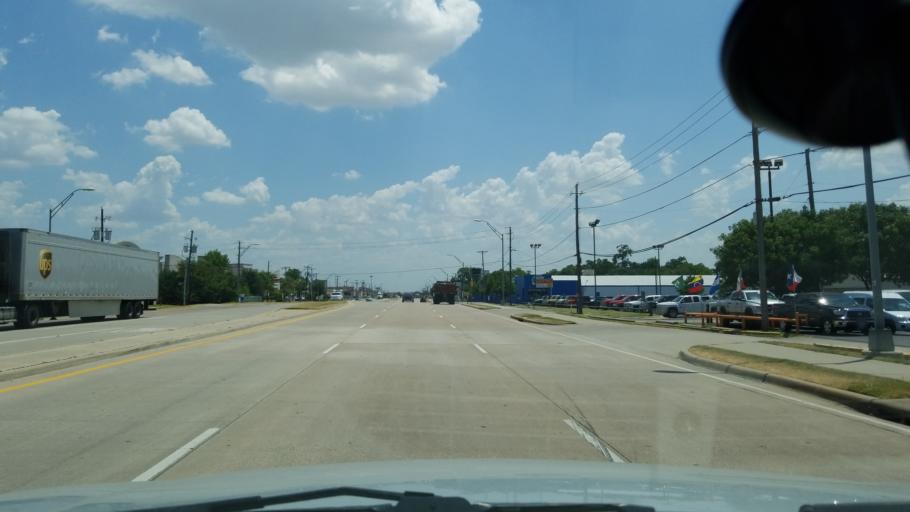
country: US
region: Texas
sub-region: Dallas County
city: Farmers Branch
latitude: 32.9026
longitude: -96.8936
